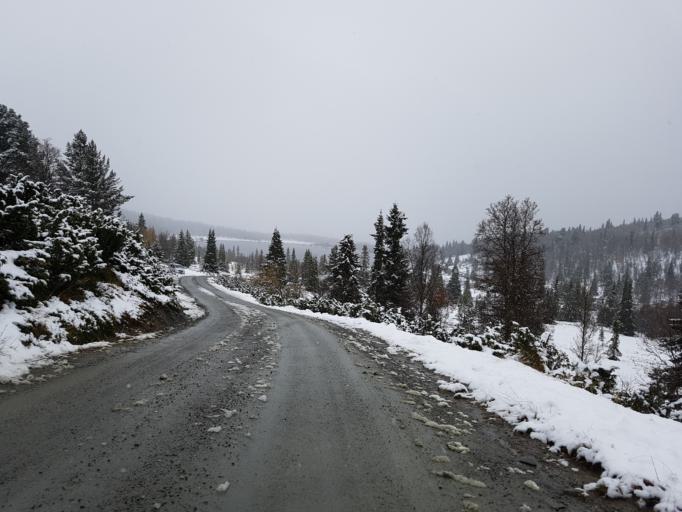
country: NO
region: Oppland
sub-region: Sel
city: Otta
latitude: 61.7977
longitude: 9.7129
